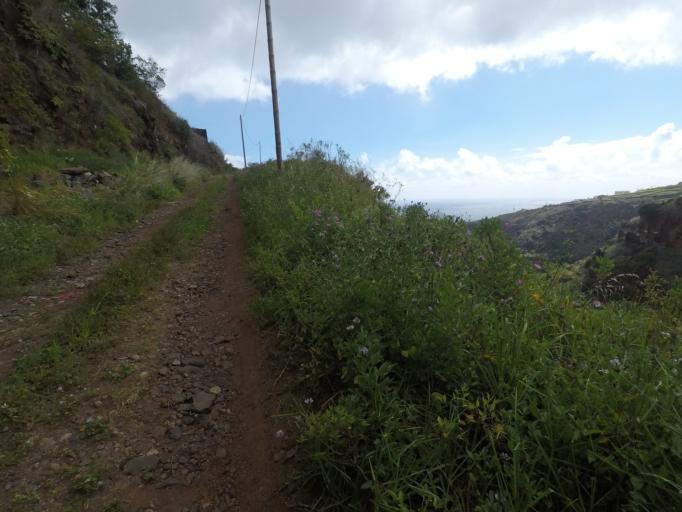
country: PT
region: Madeira
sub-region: Calheta
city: Estreito da Calheta
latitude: 32.7293
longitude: -17.1798
